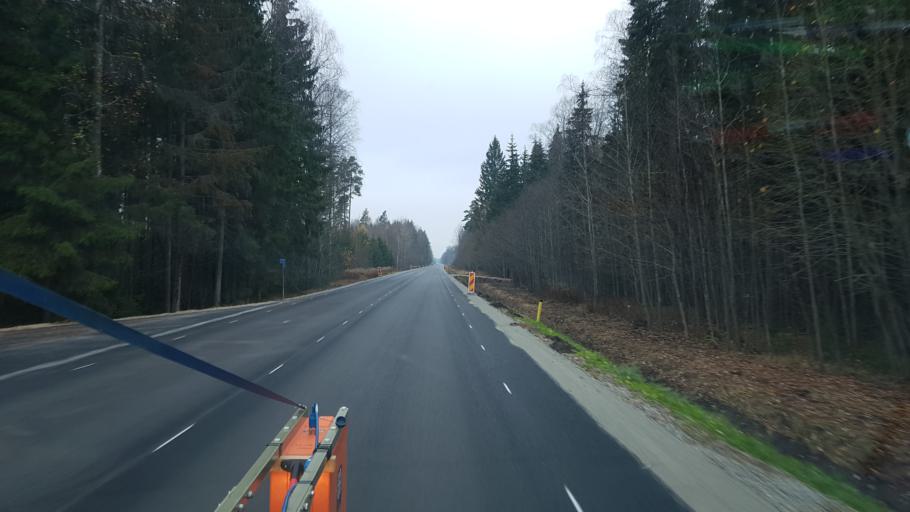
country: EE
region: Paernumaa
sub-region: Vaendra vald (alev)
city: Vandra
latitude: 58.8307
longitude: 25.1030
